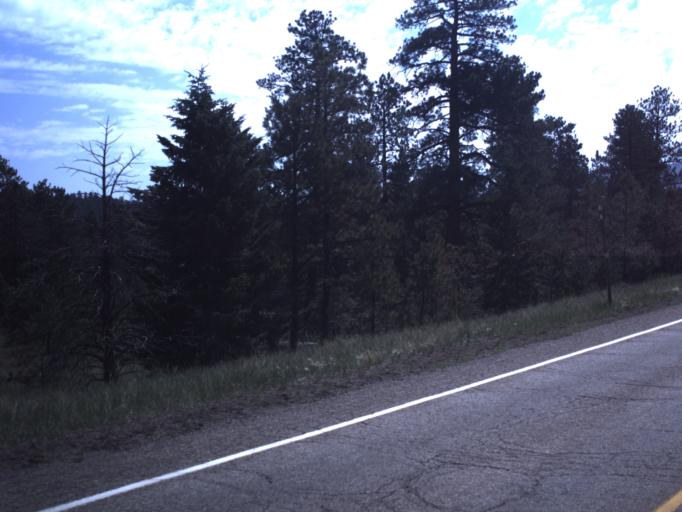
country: US
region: Utah
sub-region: Daggett County
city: Manila
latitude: 40.8532
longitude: -109.6764
